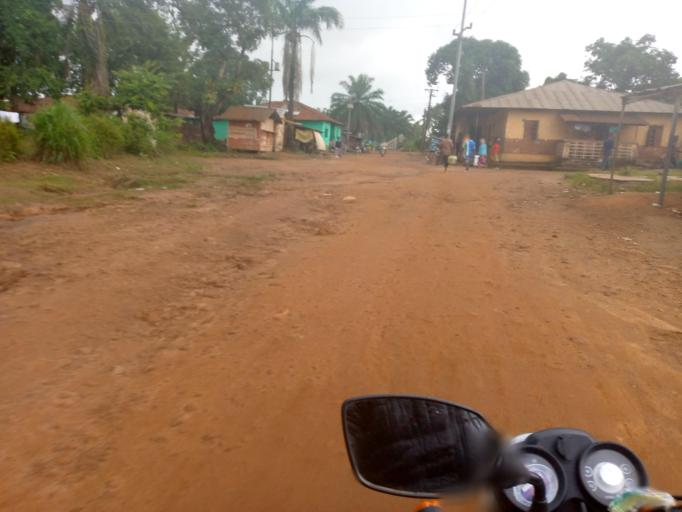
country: SL
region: Eastern Province
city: Kenema
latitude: 7.8845
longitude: -11.1820
